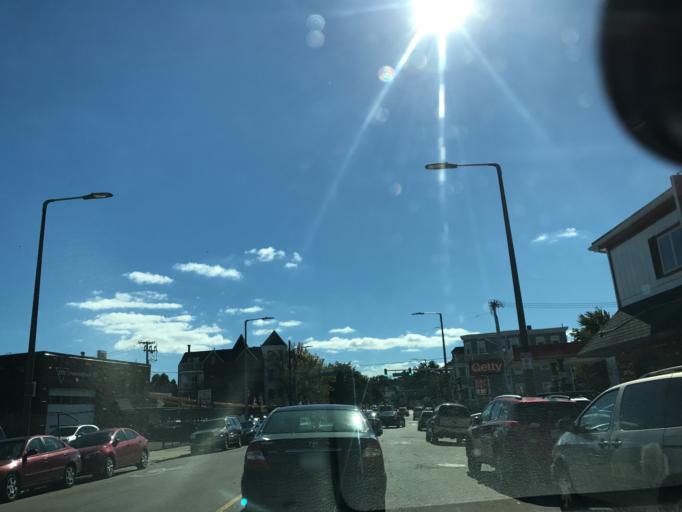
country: US
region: Massachusetts
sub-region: Suffolk County
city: South Boston
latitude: 42.2988
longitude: -71.0576
